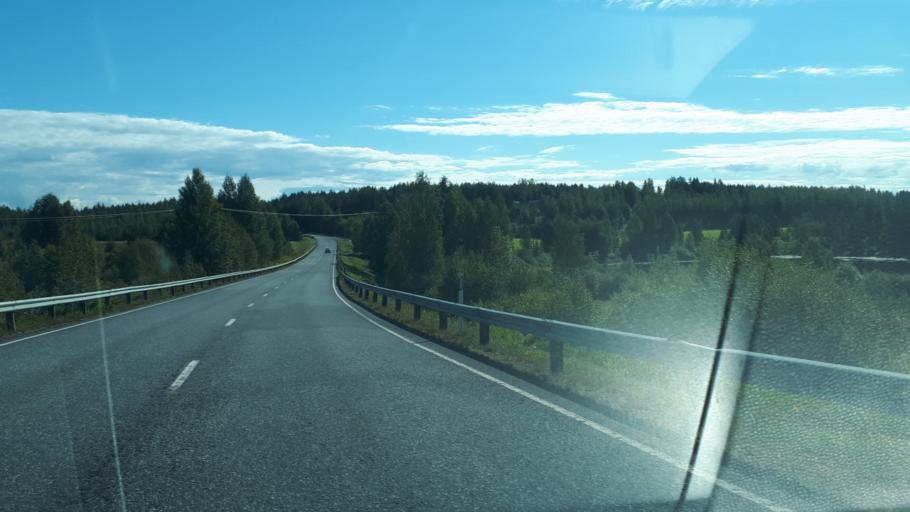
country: FI
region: Northern Savo
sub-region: Ylae-Savo
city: Vieremae
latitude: 63.6141
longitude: 26.8904
